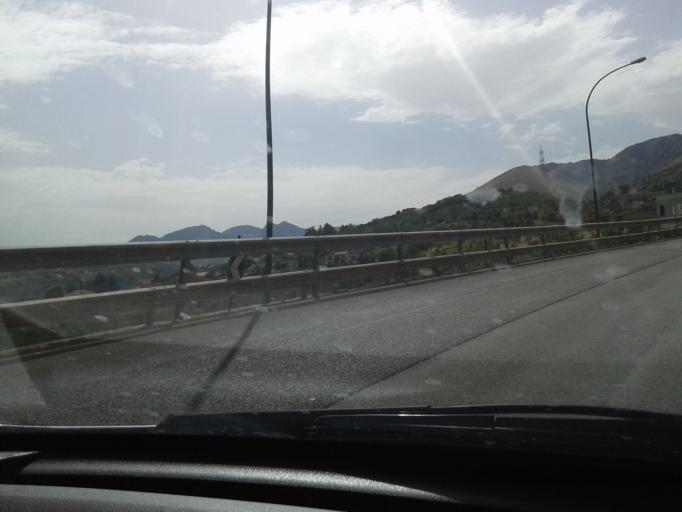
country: IT
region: Sicily
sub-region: Palermo
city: Monreale
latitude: 38.0744
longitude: 13.2861
